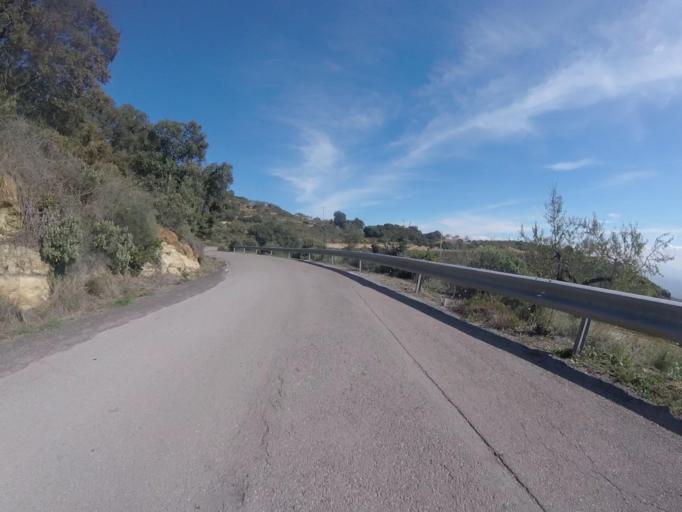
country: ES
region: Valencia
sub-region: Provincia de Castello
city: Sarratella
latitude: 40.3056
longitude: 0.0306
